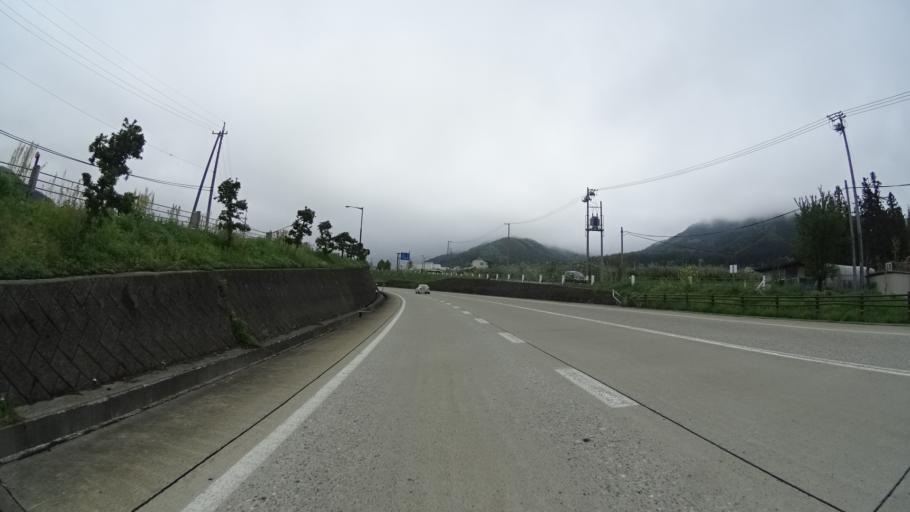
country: JP
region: Nagano
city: Nakano
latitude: 36.7354
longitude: 138.4129
